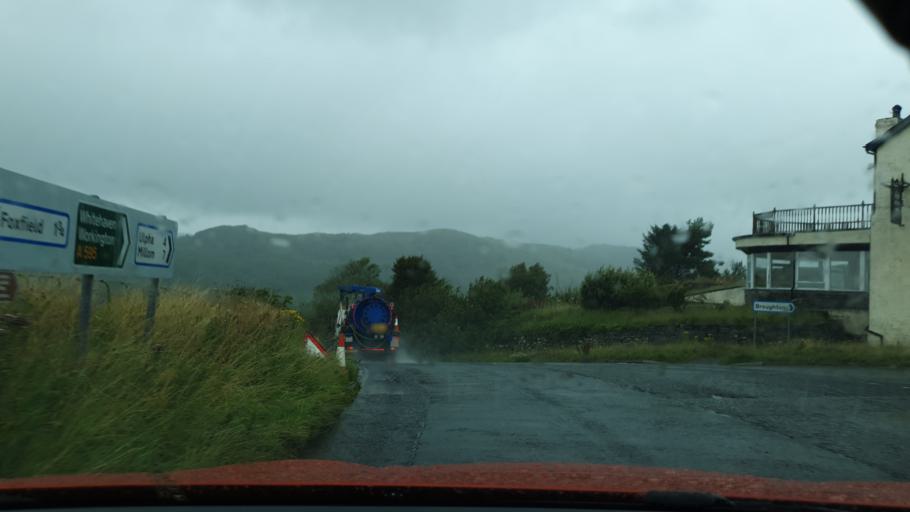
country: GB
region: England
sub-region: Cumbria
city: Millom
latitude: 54.2784
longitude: -3.2189
